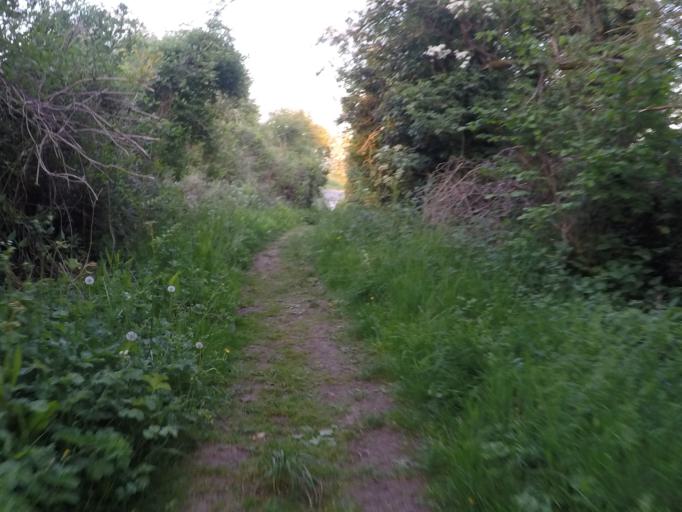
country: GB
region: England
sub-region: Oxfordshire
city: Witney
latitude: 51.8287
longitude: -1.5040
